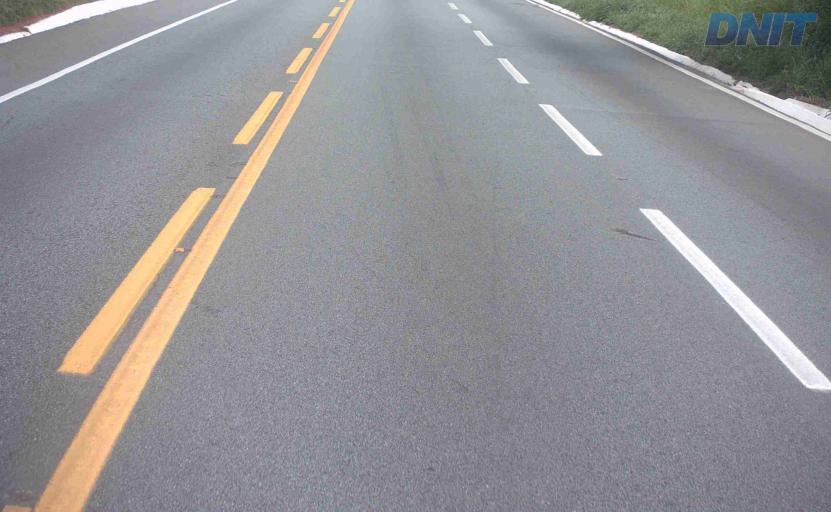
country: BR
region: Minas Gerais
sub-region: Santa Luzia
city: Santa Luzia
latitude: -19.7982
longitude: -43.7486
